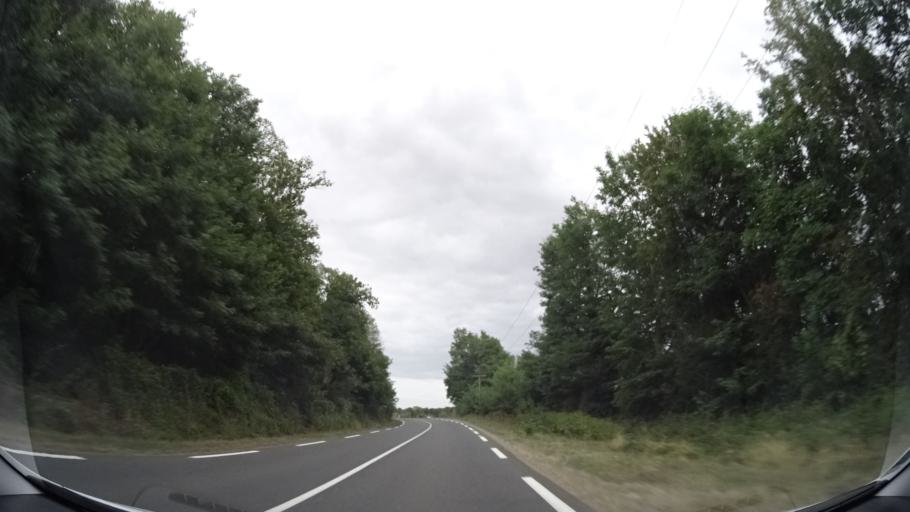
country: FR
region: Centre
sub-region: Departement du Loiret
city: Douchy
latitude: 47.9460
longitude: 3.0335
